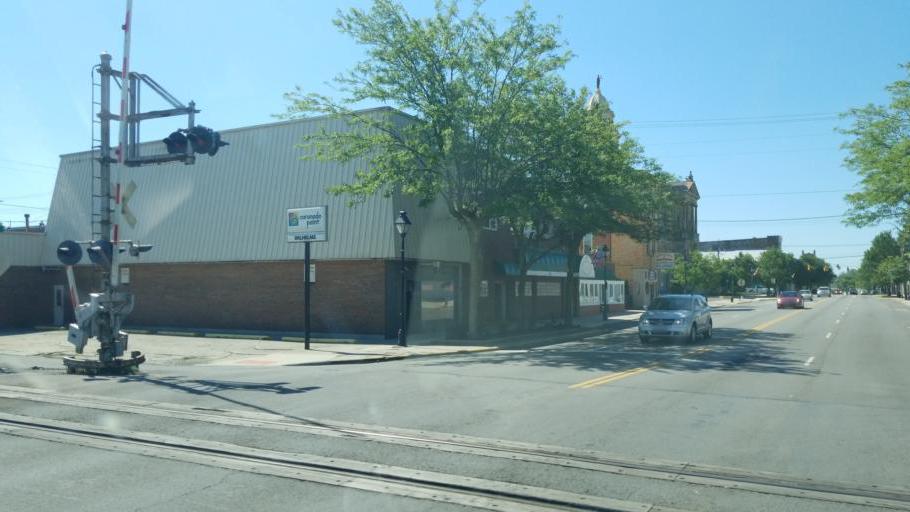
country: US
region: Ohio
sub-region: Marion County
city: Marion
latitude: 40.5901
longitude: -83.1290
